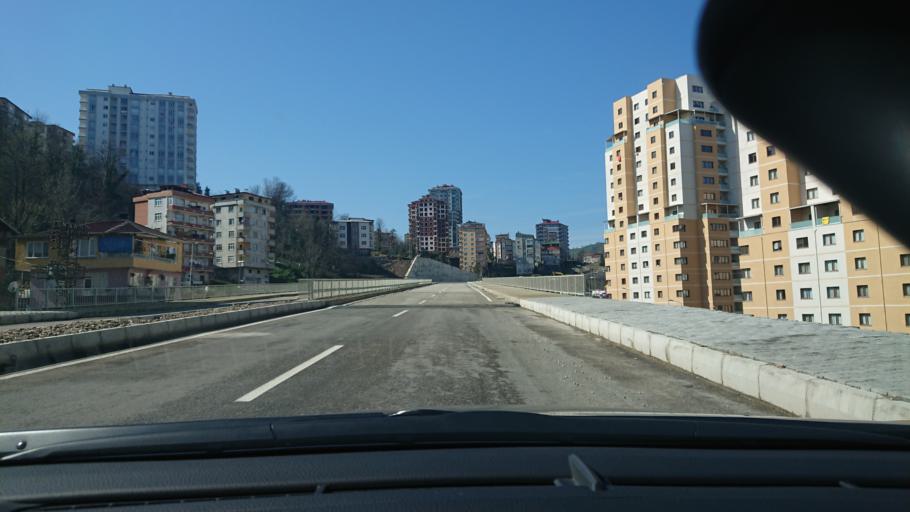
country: TR
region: Rize
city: Rize
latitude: 41.0155
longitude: 40.5165
